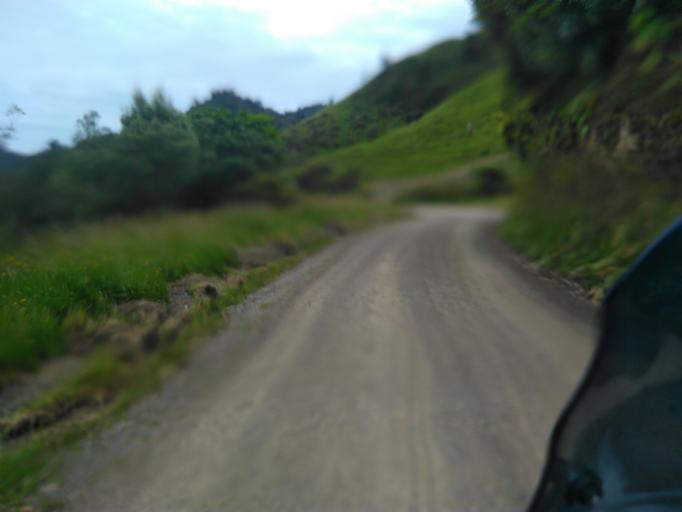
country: NZ
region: Bay of Plenty
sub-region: Opotiki District
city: Opotiki
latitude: -38.1016
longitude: 177.4894
